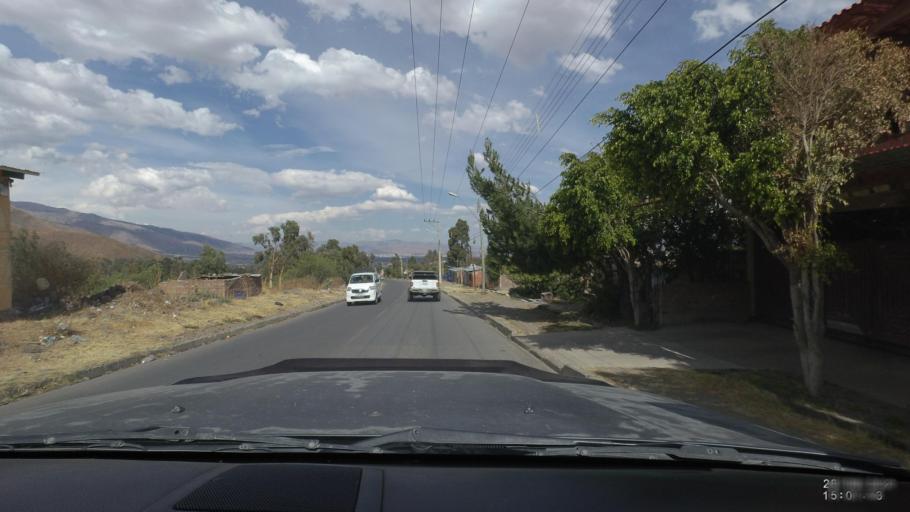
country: BO
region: Cochabamba
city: Cochabamba
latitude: -17.3115
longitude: -66.2905
